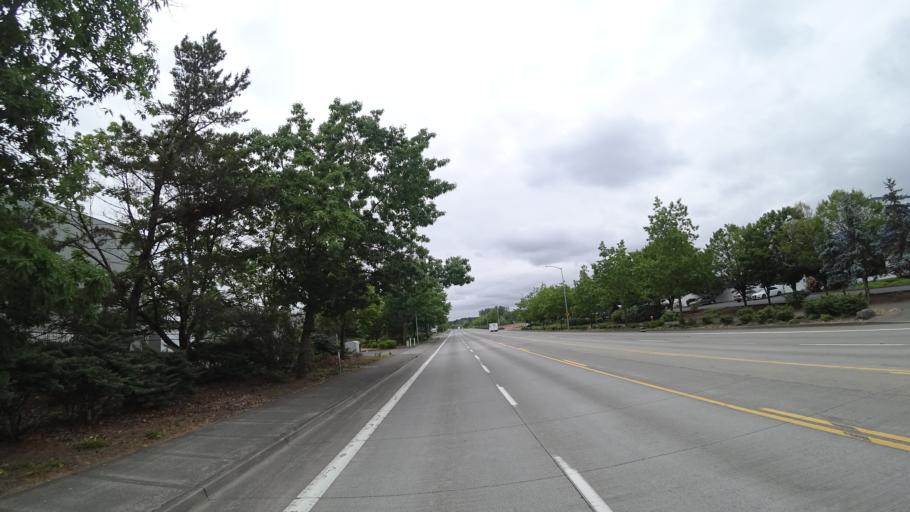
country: US
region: Washington
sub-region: Clark County
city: Vancouver
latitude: 45.6256
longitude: -122.7366
